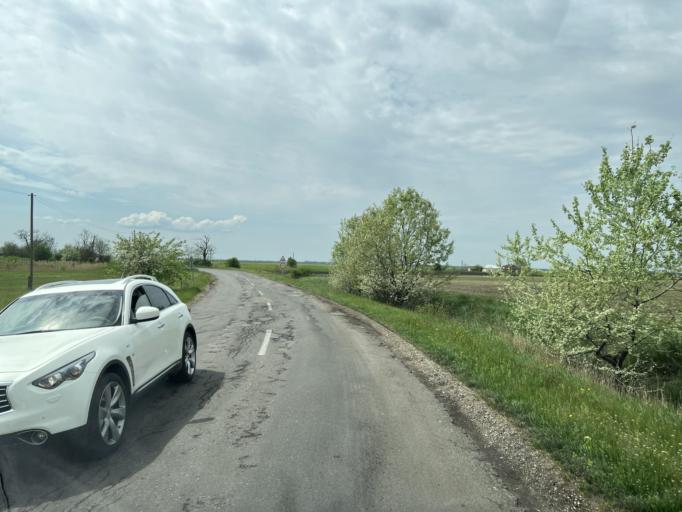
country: HU
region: Pest
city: Abony
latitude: 47.1704
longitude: 19.9788
